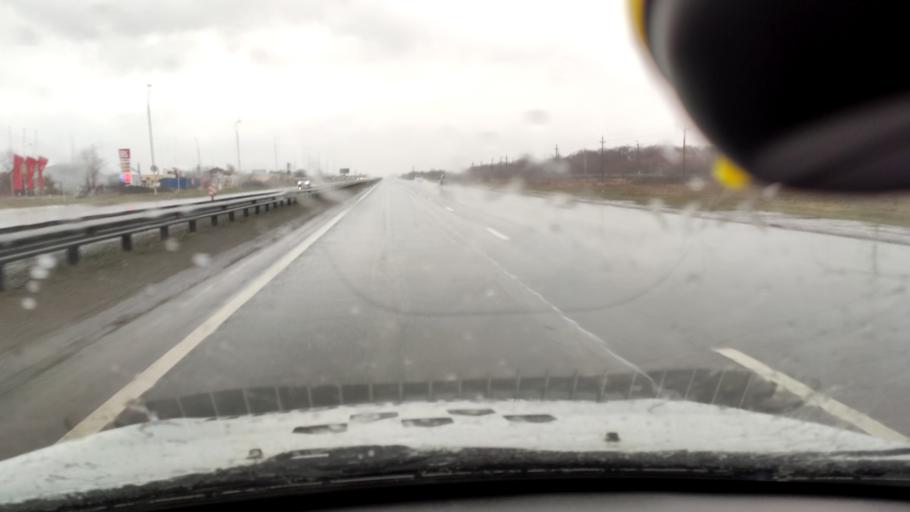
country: RU
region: Samara
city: Tol'yatti
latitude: 53.5708
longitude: 49.3845
